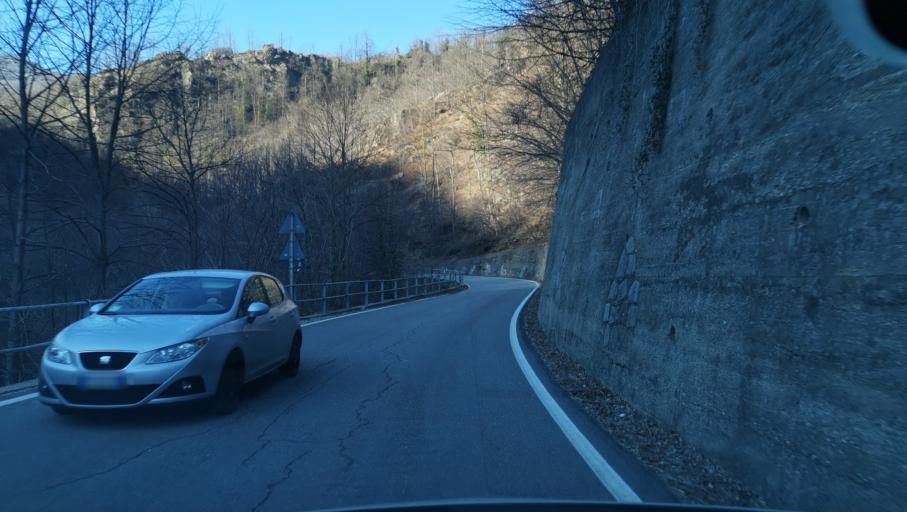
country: IT
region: Piedmont
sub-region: Provincia di Torino
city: Rora
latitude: 44.7885
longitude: 7.2050
